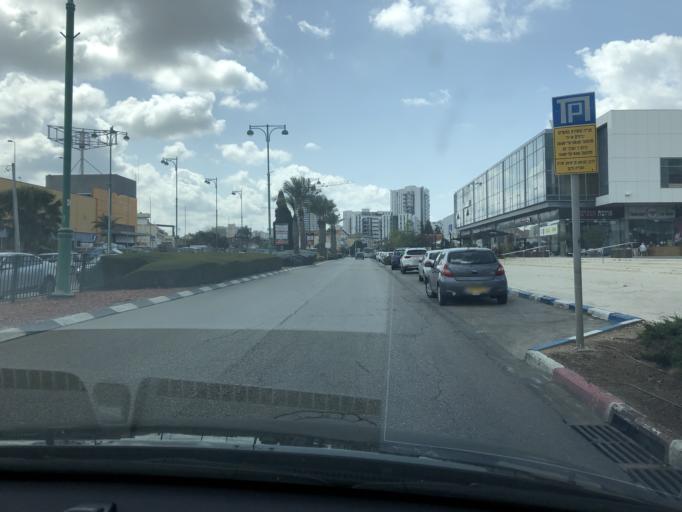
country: IL
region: Haifa
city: Hadera
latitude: 32.4407
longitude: 34.9316
